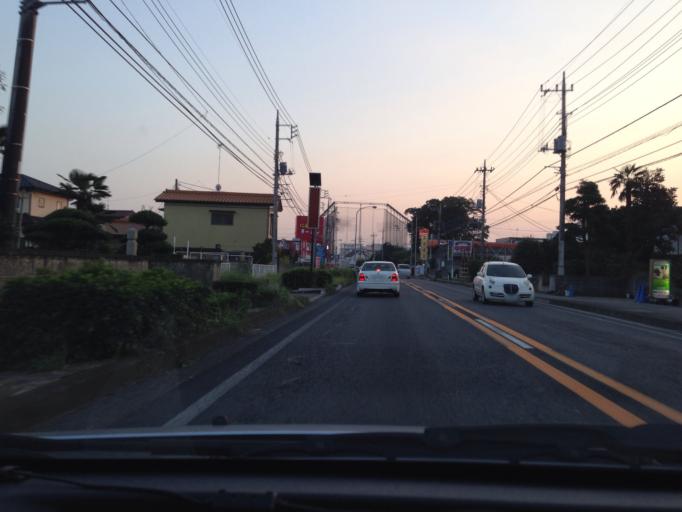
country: JP
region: Ibaraki
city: Ishioka
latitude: 36.1279
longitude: 140.2195
